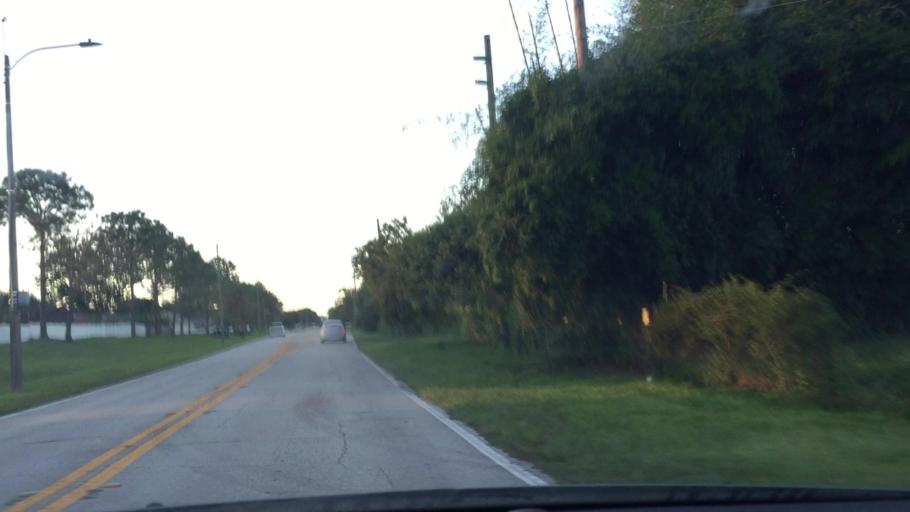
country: US
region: Florida
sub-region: Osceola County
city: Saint Cloud
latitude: 28.2606
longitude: -81.3095
